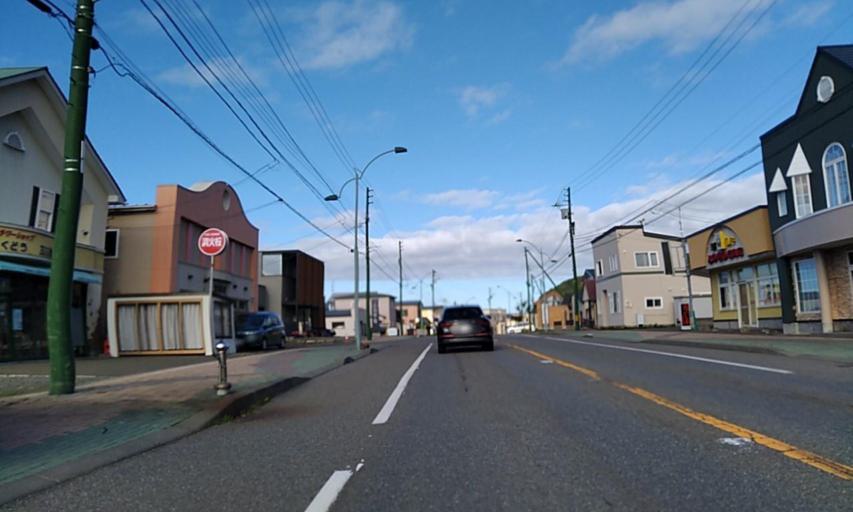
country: JP
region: Hokkaido
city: Shizunai-furukawacho
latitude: 42.2486
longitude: 142.5561
